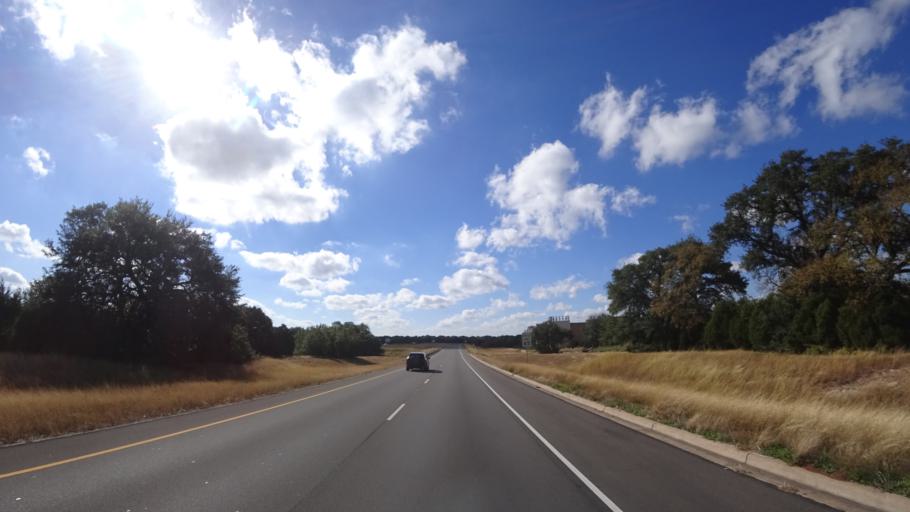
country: US
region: Texas
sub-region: Travis County
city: Shady Hollow
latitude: 30.2001
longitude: -97.8674
